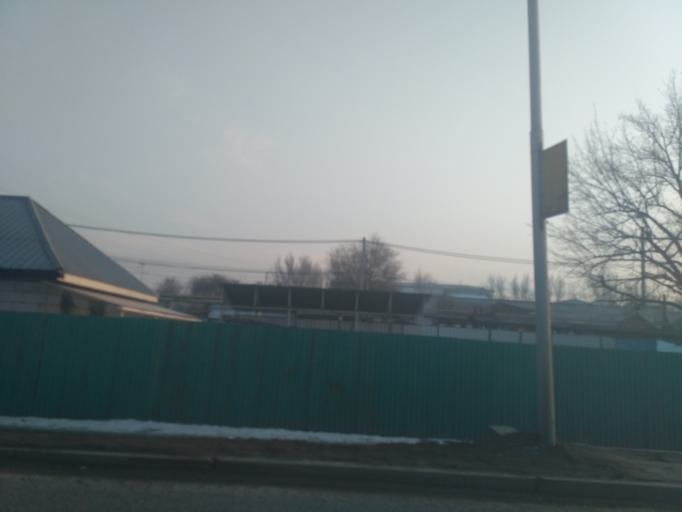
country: KZ
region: Almaty Qalasy
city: Almaty
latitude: 43.2500
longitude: 76.8491
